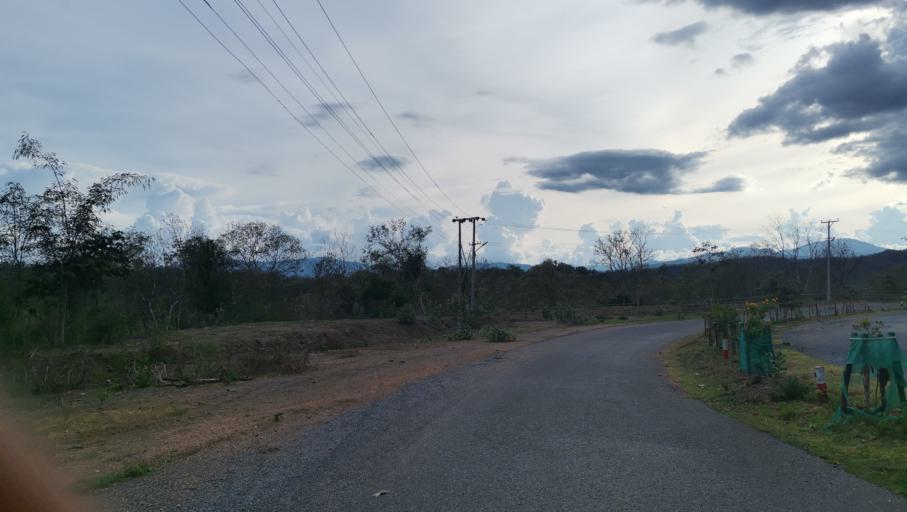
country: MM
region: Magway
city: Minbu
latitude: 20.1050
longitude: 94.5457
